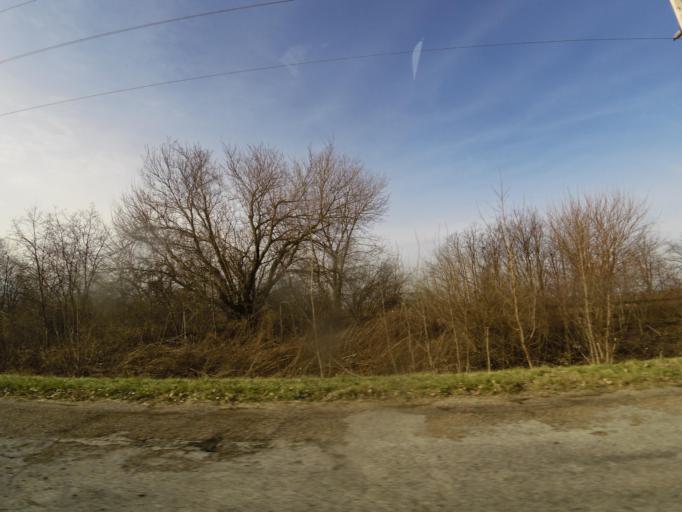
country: US
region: Illinois
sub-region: Macon County
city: Macon
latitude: 39.7698
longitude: -88.9823
